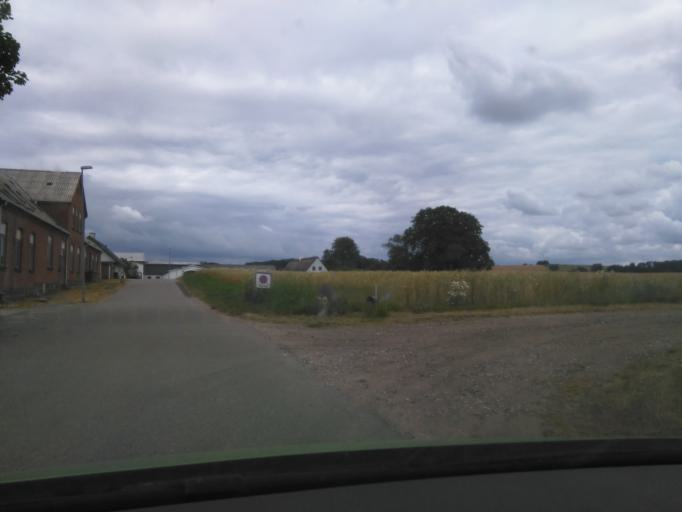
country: DK
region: Central Jutland
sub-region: Odder Kommune
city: Odder
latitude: 55.9999
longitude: 10.1606
